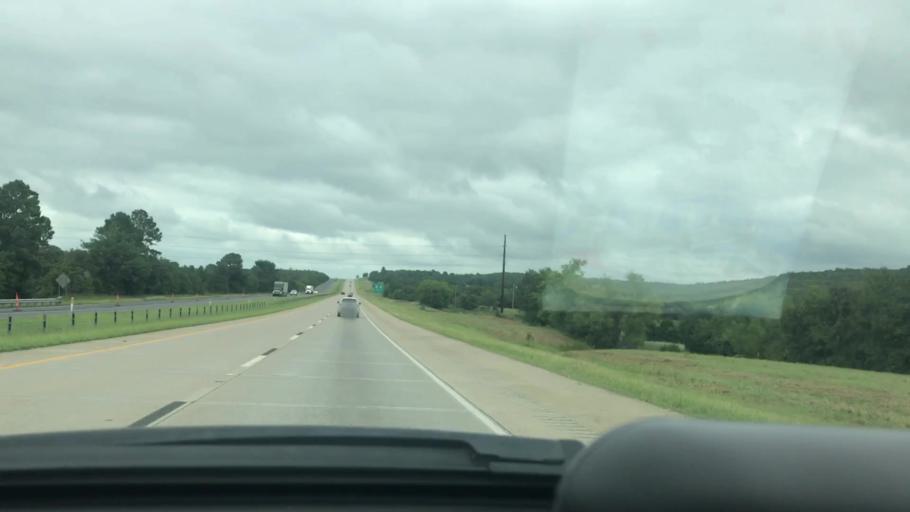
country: US
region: Oklahoma
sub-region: Pittsburg County
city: Krebs
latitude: 34.9756
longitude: -95.7232
